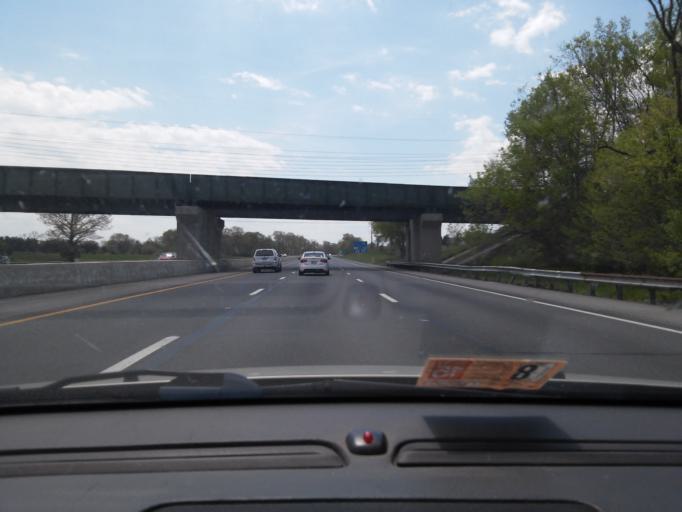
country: US
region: West Virginia
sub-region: Berkeley County
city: Martinsburg
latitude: 39.5072
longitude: -77.9392
